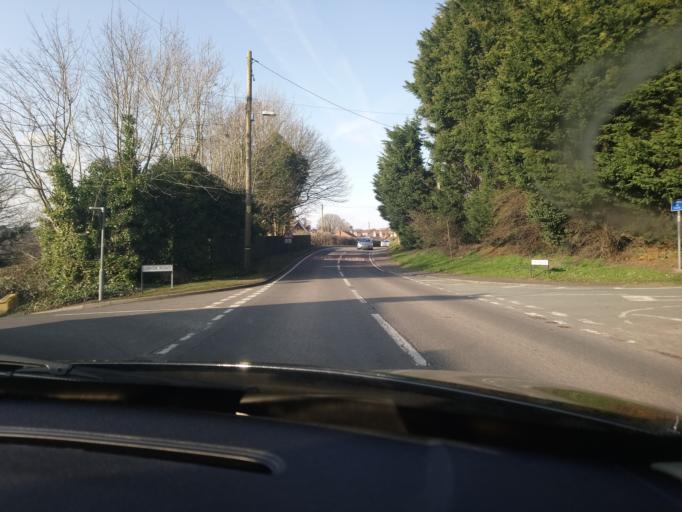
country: GB
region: England
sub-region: Shropshire
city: Clive
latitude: 52.7959
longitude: -2.7579
